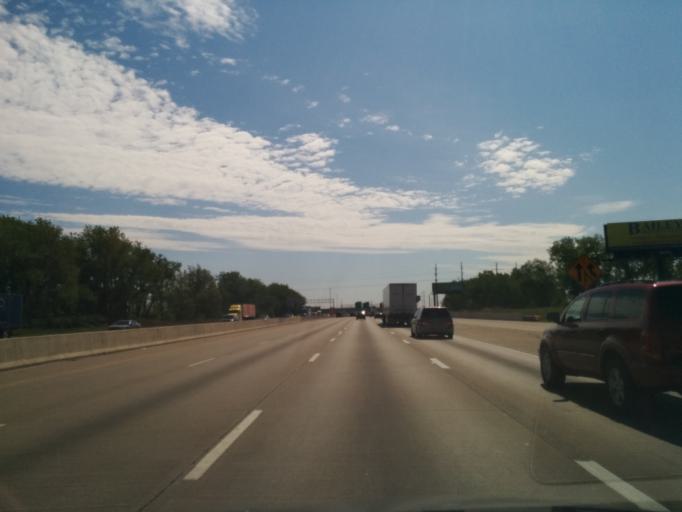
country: US
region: Indiana
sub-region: Lake County
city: Gary
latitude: 41.5673
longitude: -87.3344
